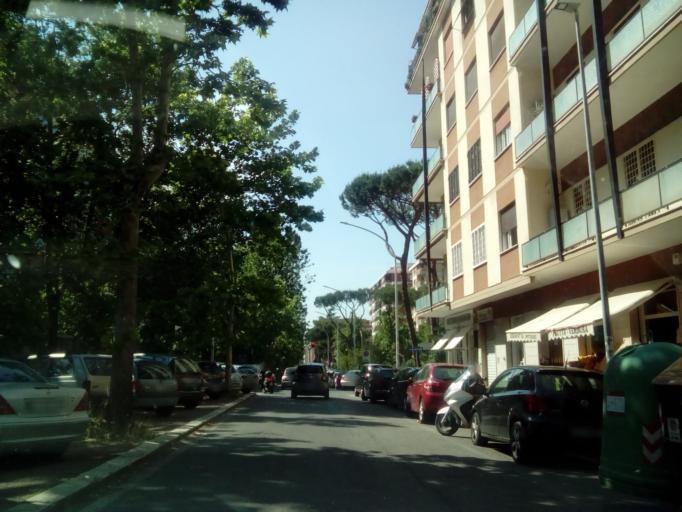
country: IT
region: Latium
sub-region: Citta metropolitana di Roma Capitale
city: Rome
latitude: 41.8540
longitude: 12.5620
